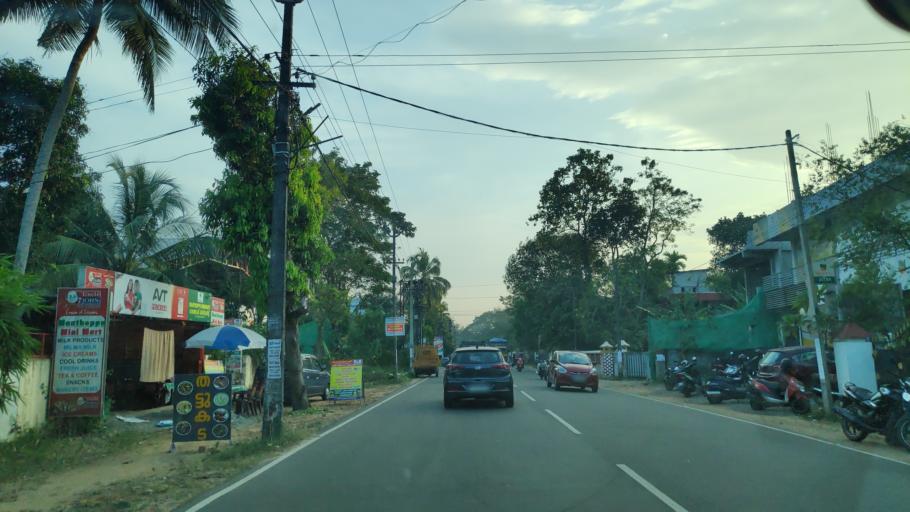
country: IN
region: Kerala
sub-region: Alappuzha
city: Shertallai
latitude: 9.6779
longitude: 76.3409
